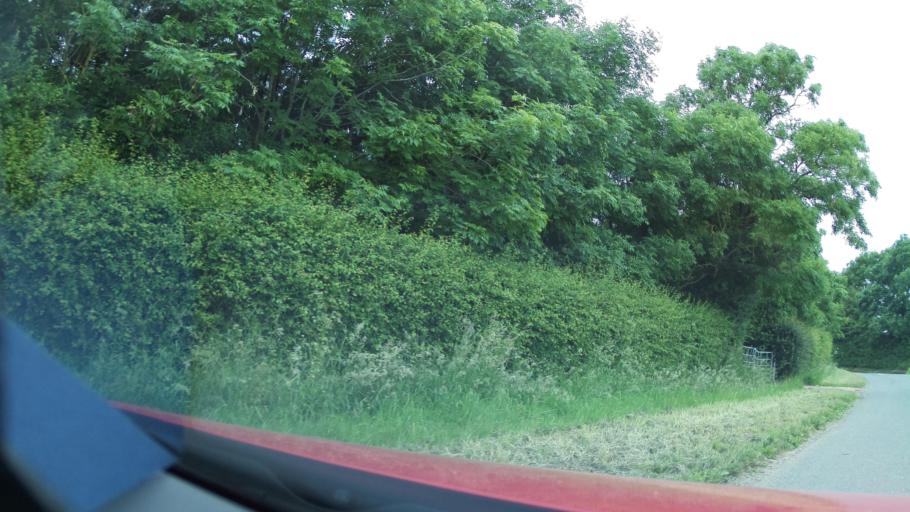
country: GB
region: England
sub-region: District of Rutland
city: Langham
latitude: 52.6807
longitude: -0.7984
